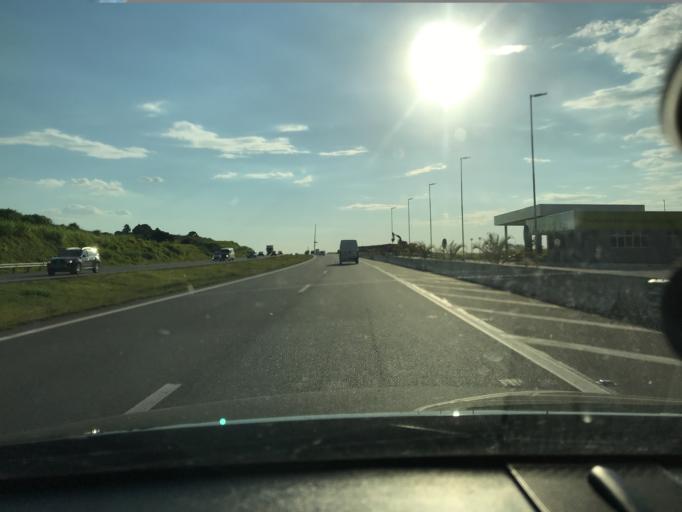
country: BR
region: Sao Paulo
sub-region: Valinhos
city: Valinhos
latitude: -22.9911
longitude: -47.0678
